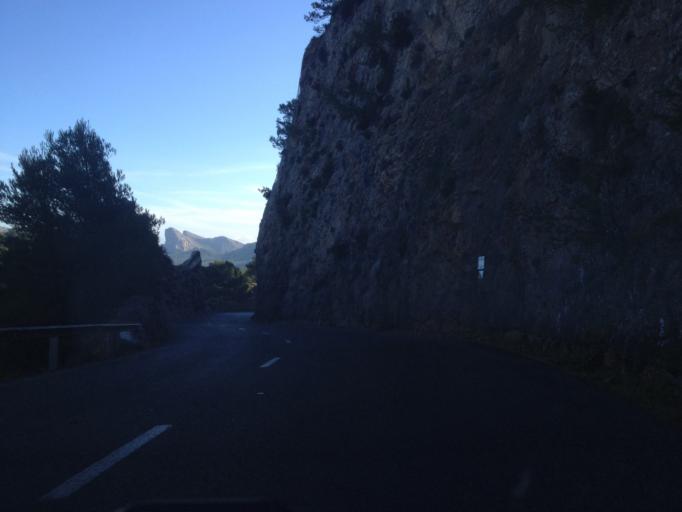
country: ES
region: Balearic Islands
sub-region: Illes Balears
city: Alcudia
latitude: 39.9305
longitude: 3.1199
